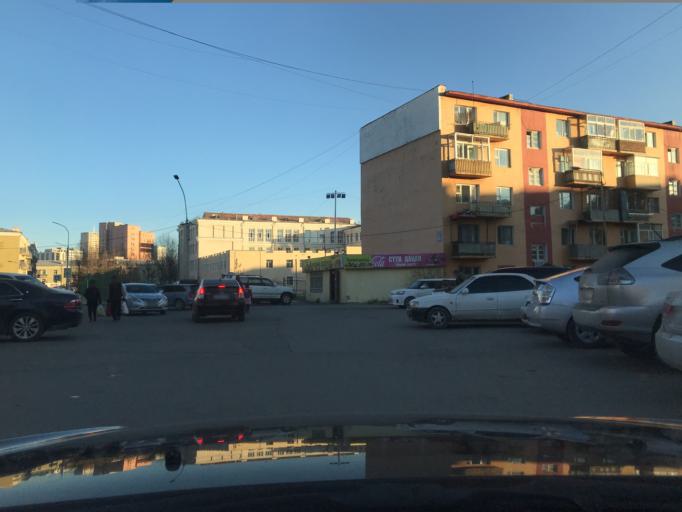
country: MN
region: Ulaanbaatar
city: Ulaanbaatar
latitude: 47.9264
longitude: 106.9100
